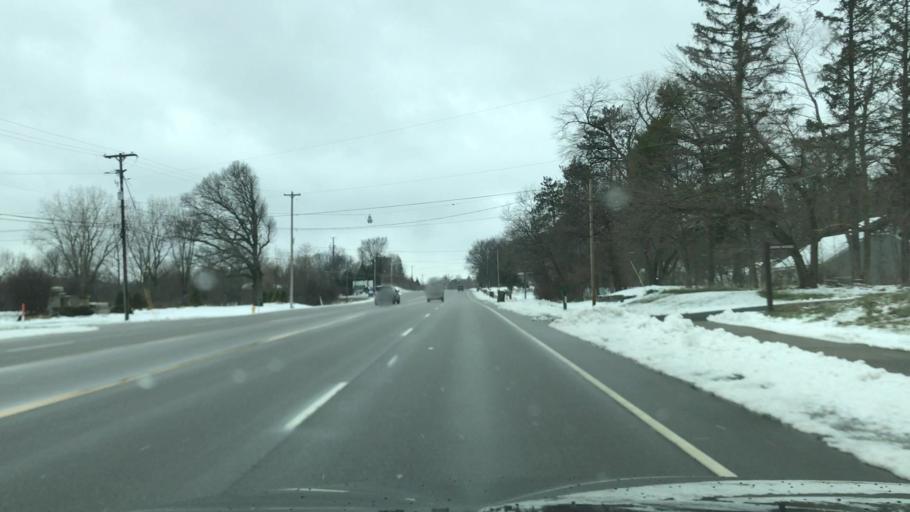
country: US
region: Michigan
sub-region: Kent County
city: Forest Hills
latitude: 42.9379
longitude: -85.5330
